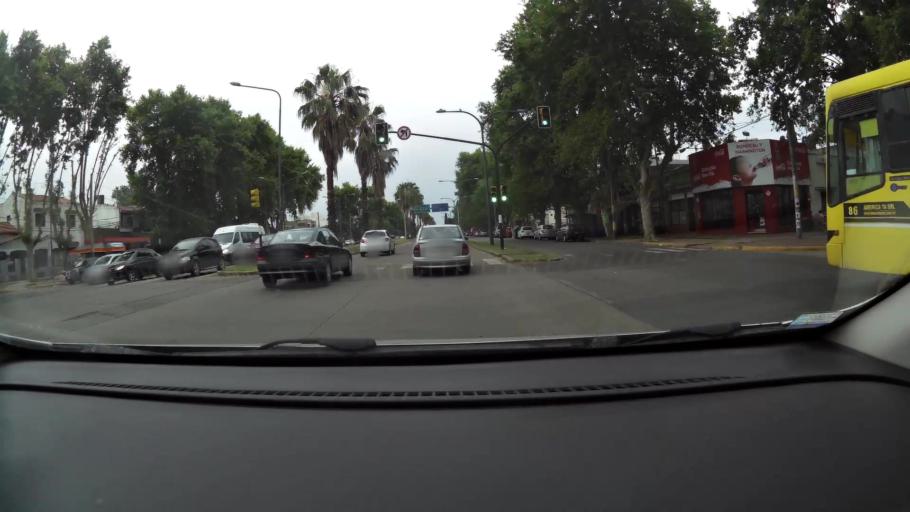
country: AR
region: Santa Fe
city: Granadero Baigorria
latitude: -32.9012
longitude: -60.6903
